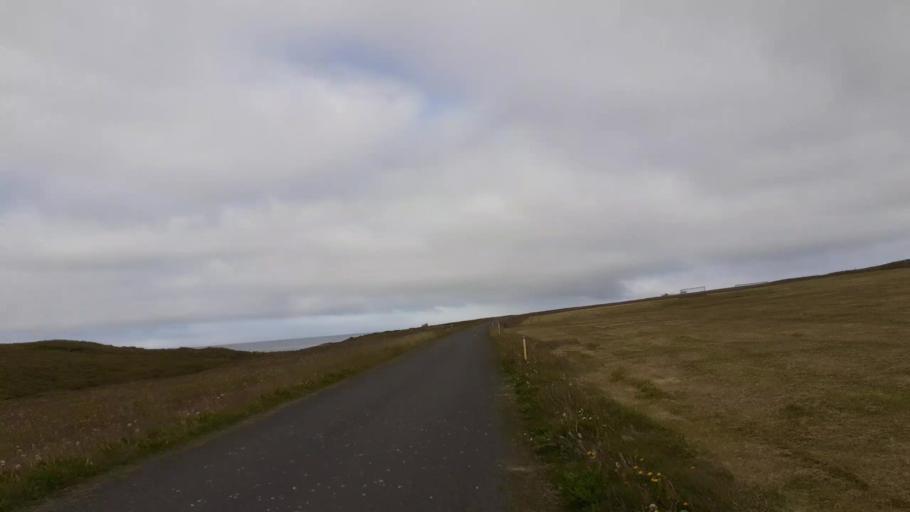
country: IS
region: Northeast
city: Dalvik
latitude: 66.5425
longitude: -18.0172
